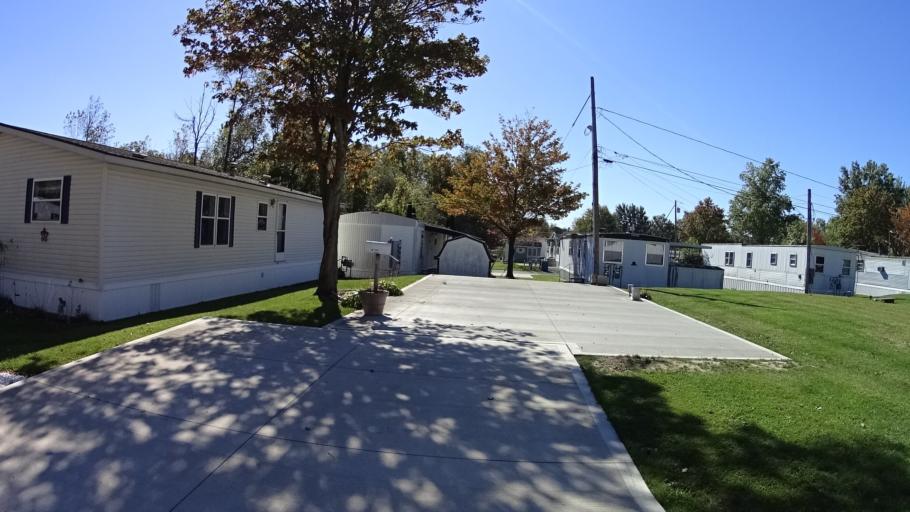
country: US
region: Ohio
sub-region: Lorain County
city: Amherst
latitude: 41.3931
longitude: -82.2492
